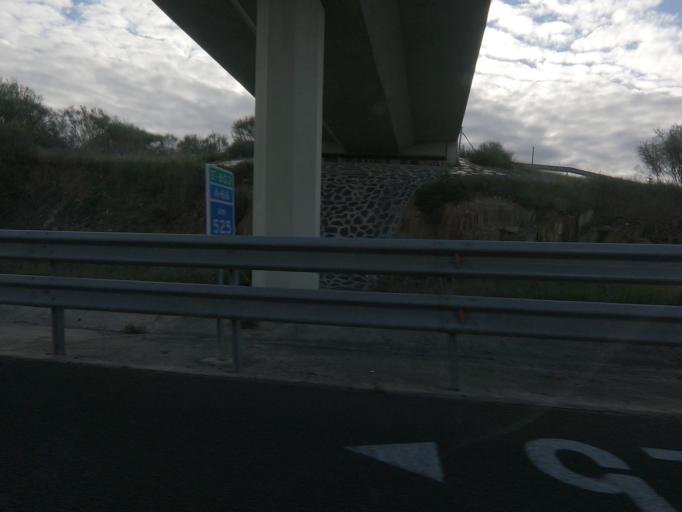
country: ES
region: Extremadura
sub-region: Provincia de Caceres
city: Hinojal
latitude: 39.6808
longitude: -6.3987
